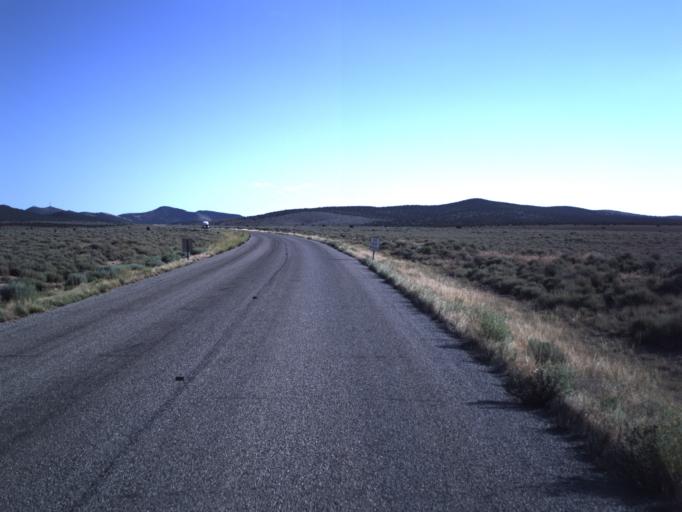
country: US
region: Utah
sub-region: Iron County
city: Enoch
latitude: 38.0012
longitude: -112.9981
